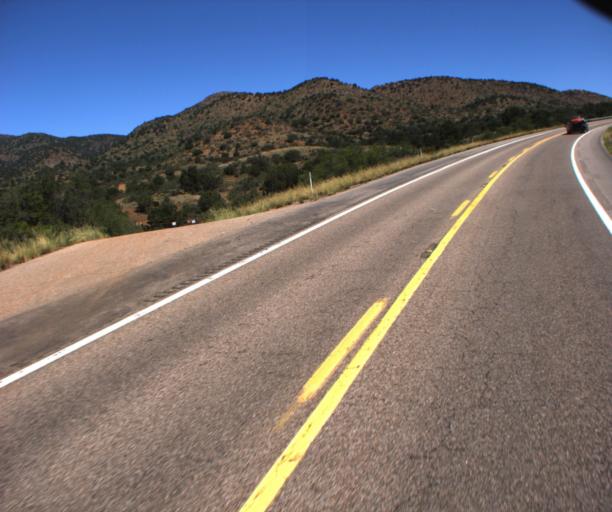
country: US
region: Arizona
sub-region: Gila County
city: Globe
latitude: 33.4927
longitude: -110.7169
